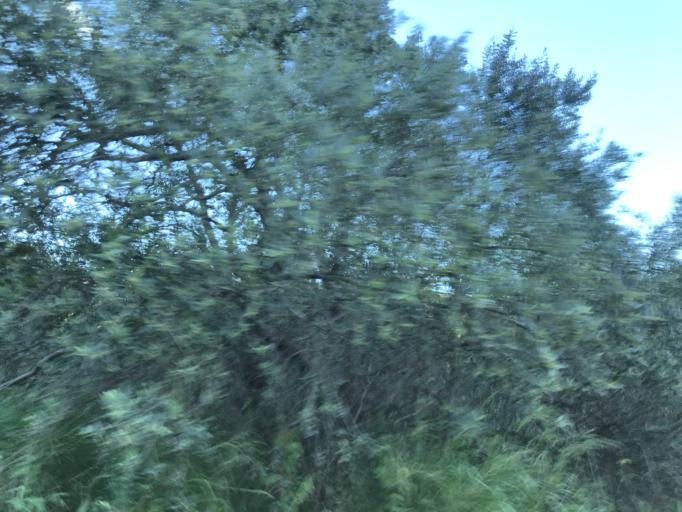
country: TR
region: Hatay
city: Buyukcat
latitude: 36.0944
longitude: 36.0616
